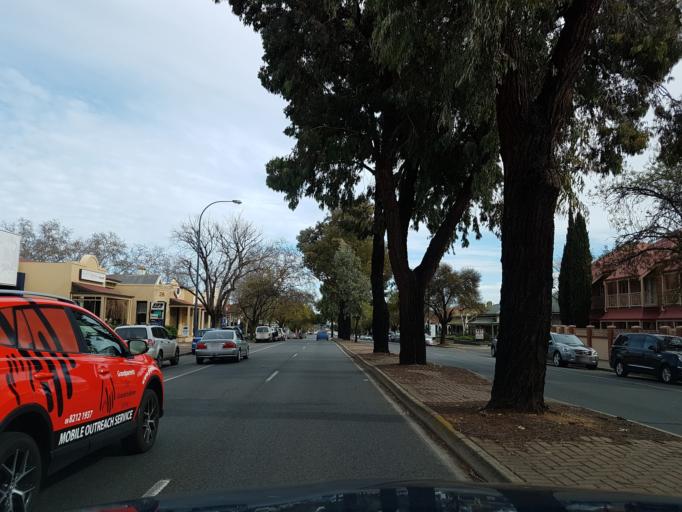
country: AU
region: South Australia
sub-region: Norwood Payneham St Peters
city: Trinity Gardens
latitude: -34.9216
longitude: 138.6265
